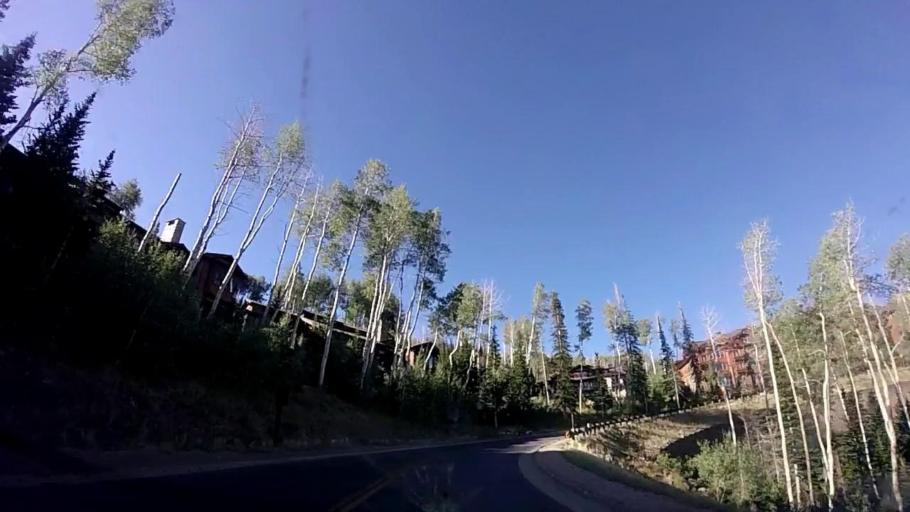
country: US
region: Utah
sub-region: Summit County
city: Park City
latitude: 40.6215
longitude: -111.5029
